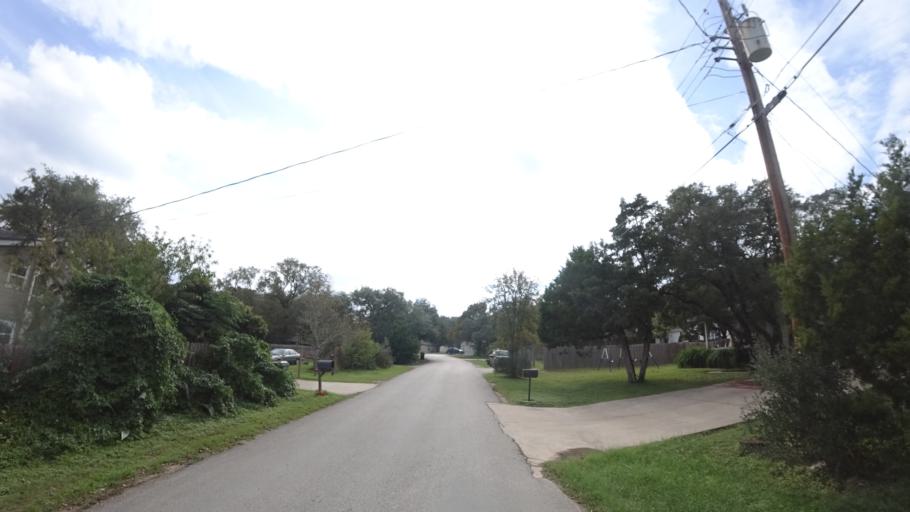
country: US
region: Texas
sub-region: Travis County
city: Hudson Bend
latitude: 30.3778
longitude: -97.9285
